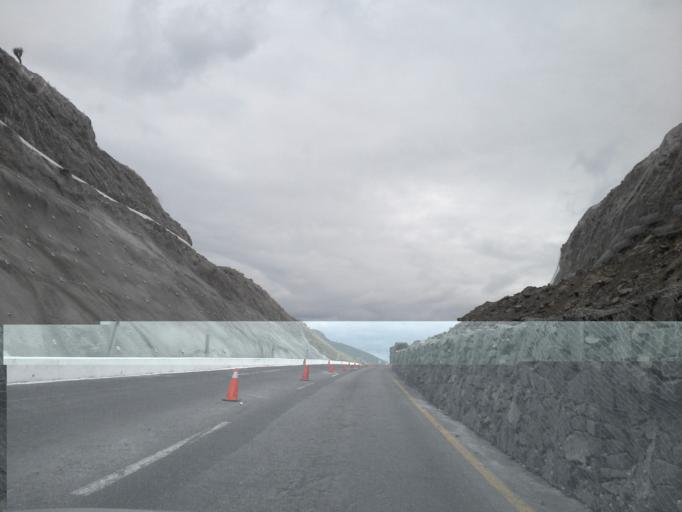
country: MX
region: Durango
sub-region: Lerdo
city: Picardias
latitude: 25.1729
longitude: -103.7200
